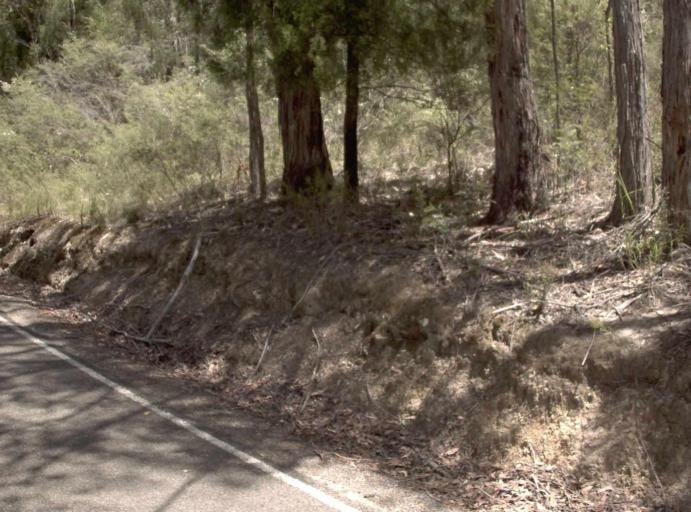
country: AU
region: Victoria
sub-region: East Gippsland
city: Lakes Entrance
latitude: -37.5781
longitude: 147.8950
